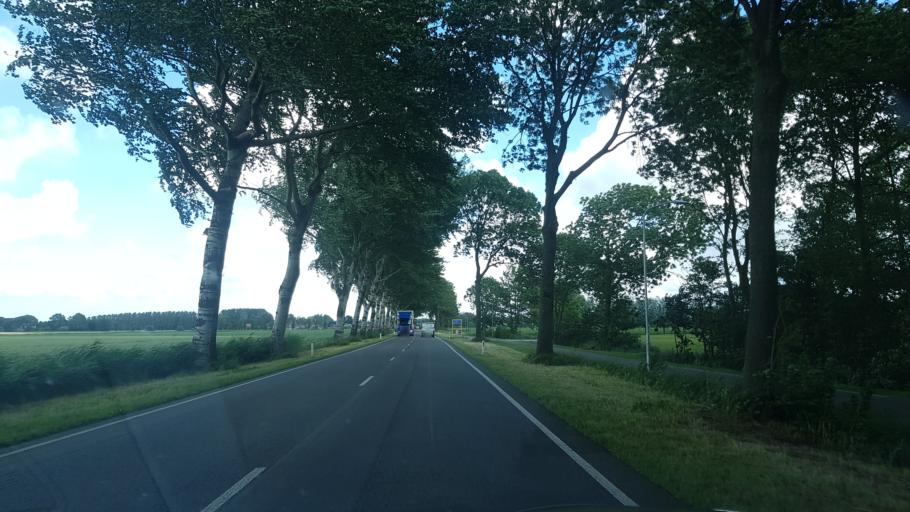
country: NL
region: Groningen
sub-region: Gemeente Winsum
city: Winsum
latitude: 53.3878
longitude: 6.5399
